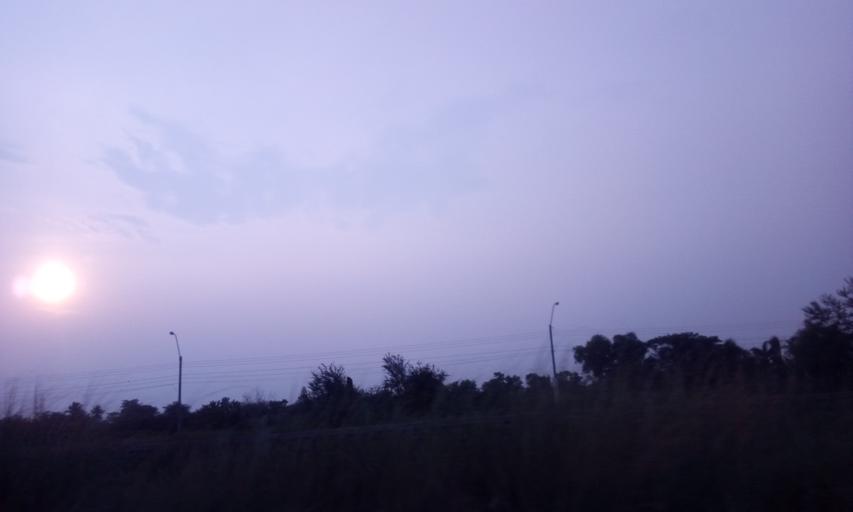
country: TH
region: Bangkok
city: Nong Chok
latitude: 13.8651
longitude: 100.8748
